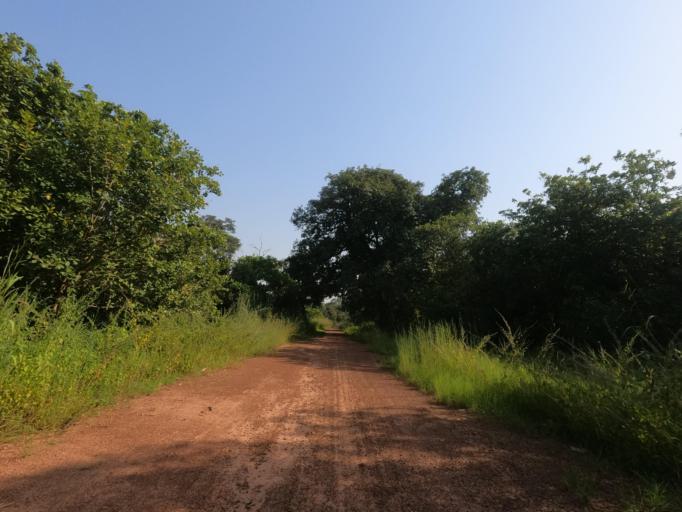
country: SN
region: Sedhiou
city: Sedhiou
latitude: 12.4415
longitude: -15.7383
